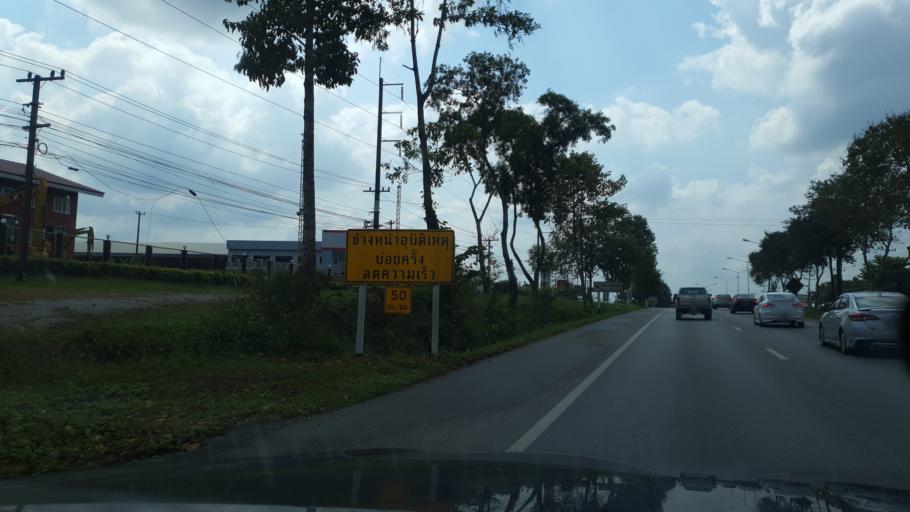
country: TH
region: Chumphon
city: Chumphon
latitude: 10.5356
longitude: 99.1165
